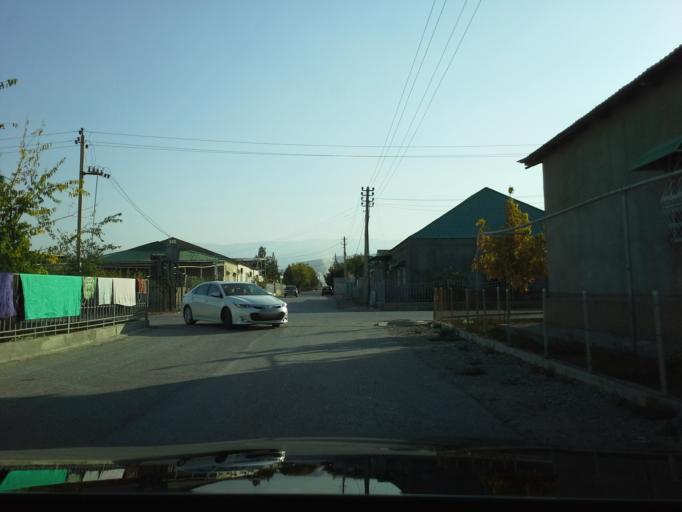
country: TM
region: Ahal
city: Abadan
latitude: 38.0490
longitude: 58.1676
